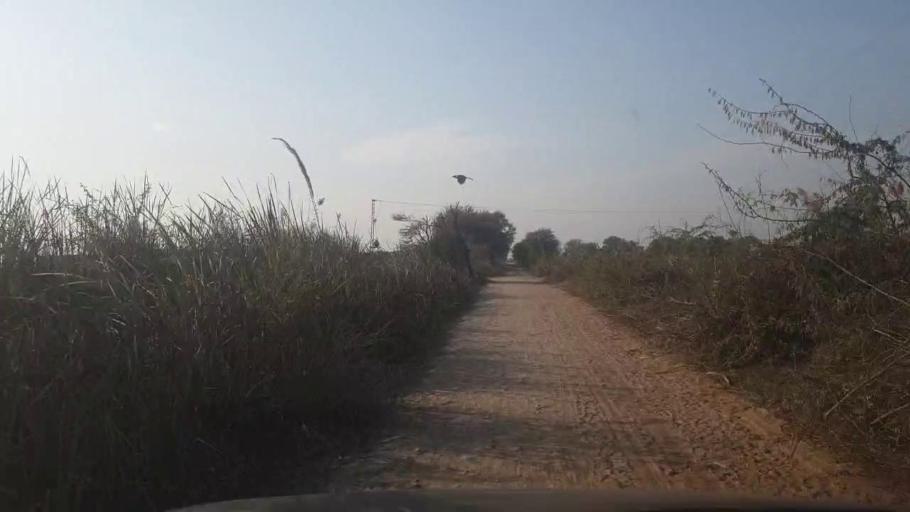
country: PK
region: Sindh
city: Sakrand
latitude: 26.0644
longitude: 68.3448
